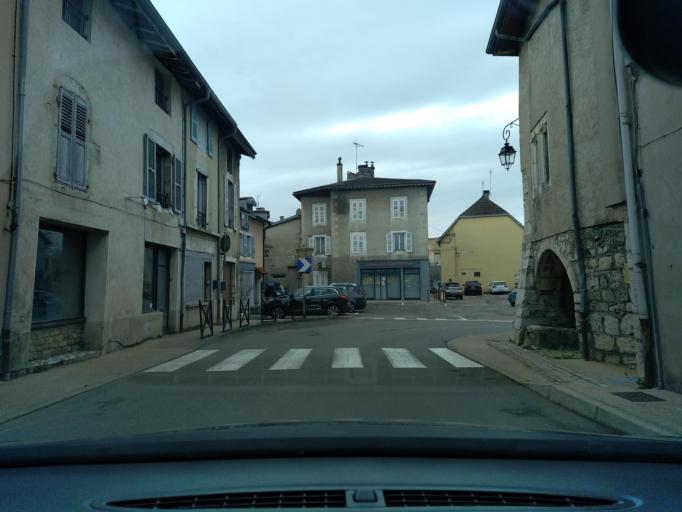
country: FR
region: Franche-Comte
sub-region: Departement du Jura
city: Arinthod
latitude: 46.3934
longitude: 5.5674
